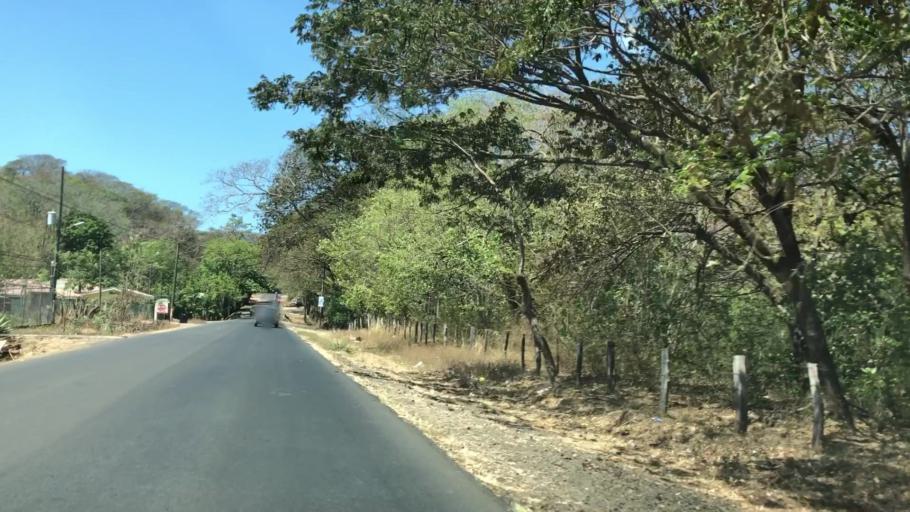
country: CR
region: Guanacaste
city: Belen
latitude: 10.3664
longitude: -85.7906
